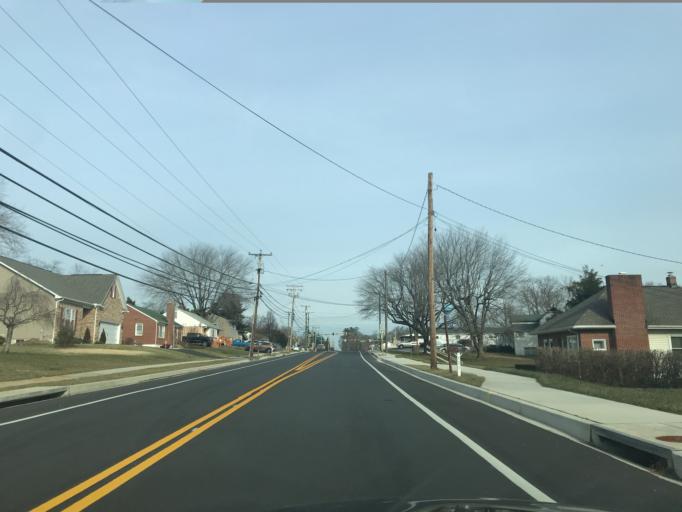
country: US
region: Maryland
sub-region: Harford County
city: Aberdeen
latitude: 39.5200
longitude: -76.1712
